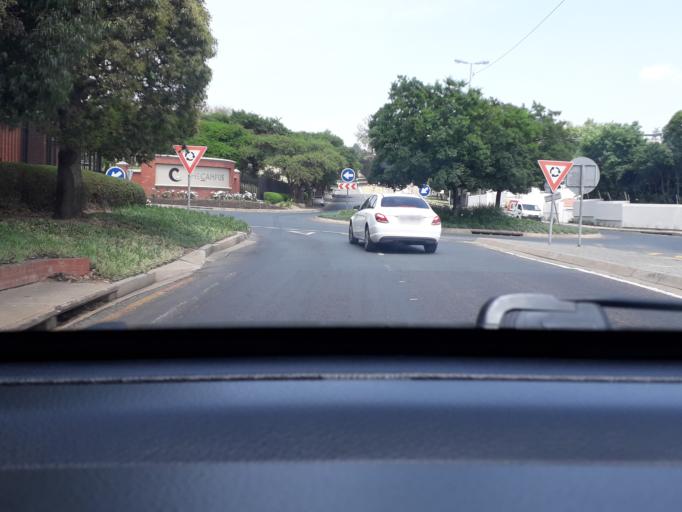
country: ZA
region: Gauteng
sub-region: City of Johannesburg Metropolitan Municipality
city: Diepsloot
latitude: -26.0395
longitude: 28.0236
